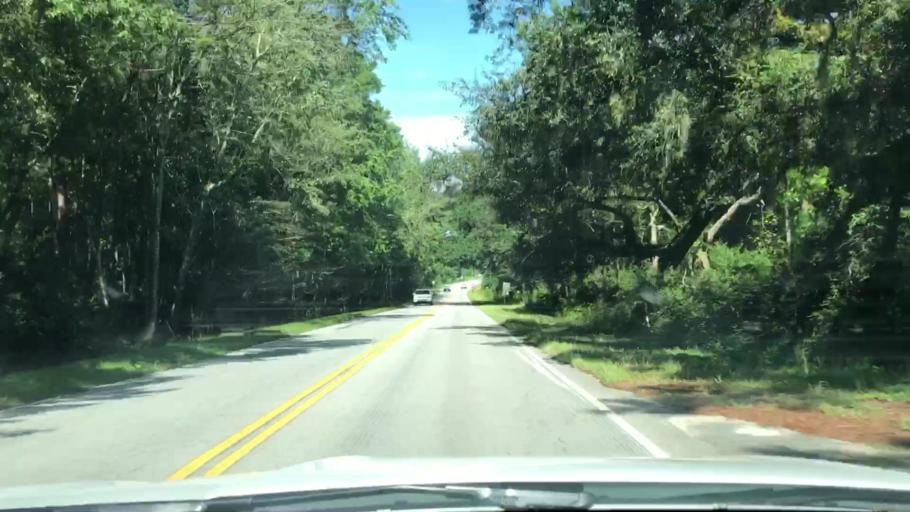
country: US
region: South Carolina
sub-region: Dorchester County
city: Centerville
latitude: 32.9459
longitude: -80.1981
